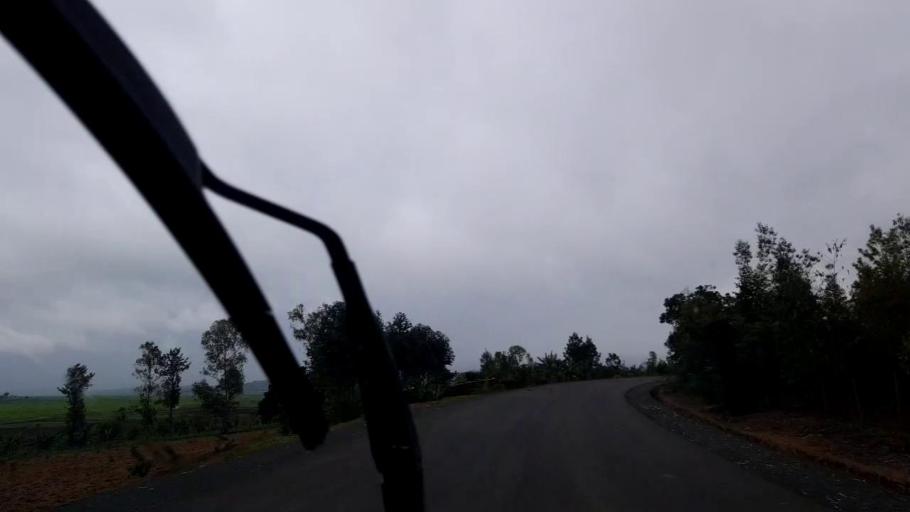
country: RW
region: Northern Province
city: Byumba
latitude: -1.4242
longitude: 30.2684
